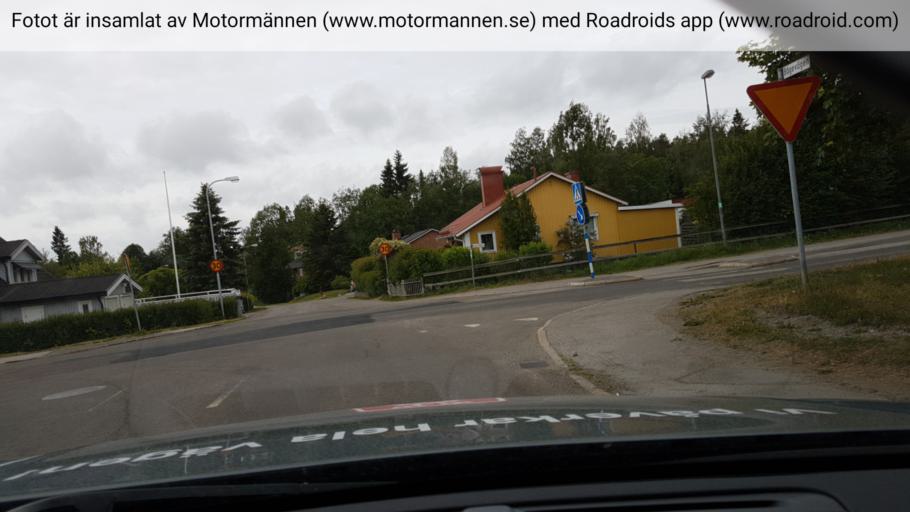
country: SE
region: Vaesternorrland
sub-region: Sundsvalls Kommun
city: Johannedal
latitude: 62.4176
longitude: 17.3405
